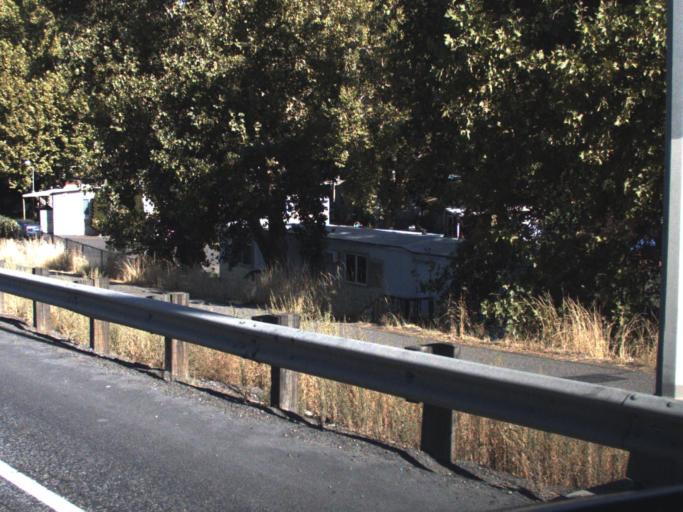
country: US
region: Washington
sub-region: Benton County
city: Kennewick
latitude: 46.2295
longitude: -119.1335
